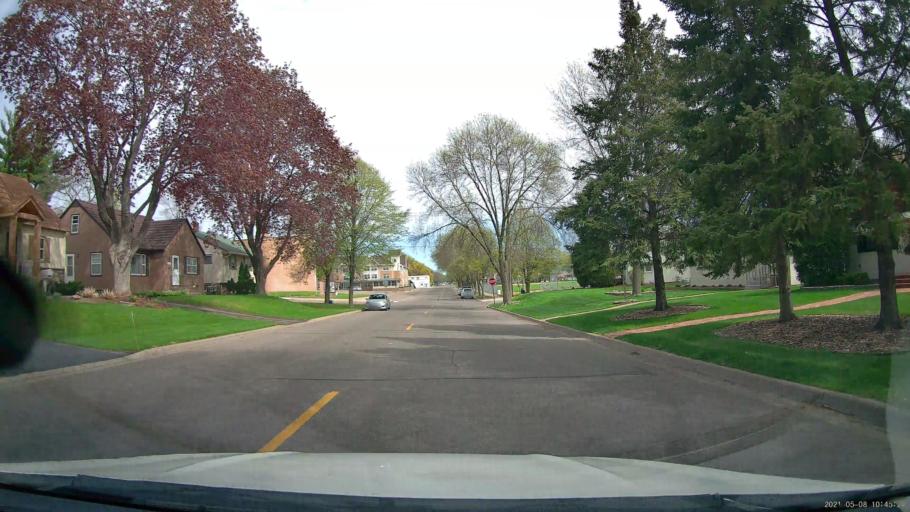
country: US
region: Minnesota
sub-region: Dakota County
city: South Saint Paul
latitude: 44.8937
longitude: -93.0526
